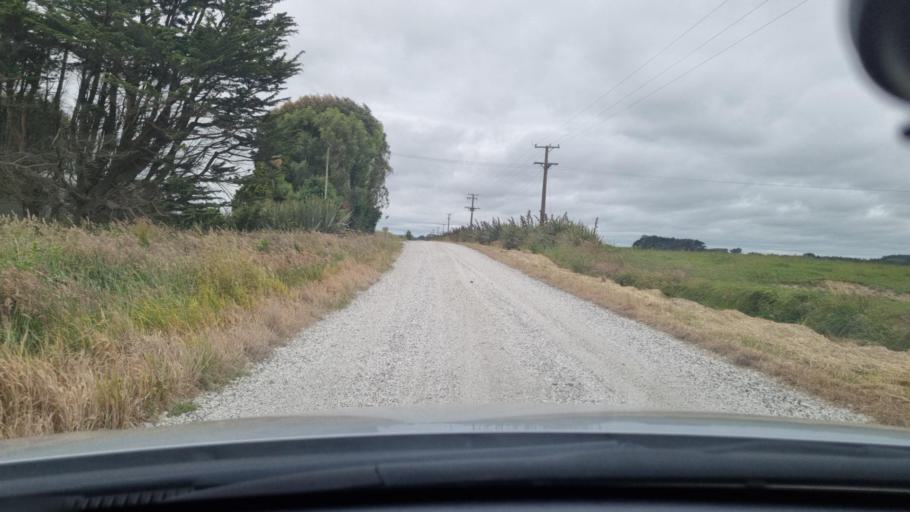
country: NZ
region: Southland
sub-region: Invercargill City
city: Invercargill
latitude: -46.3866
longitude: 168.2811
